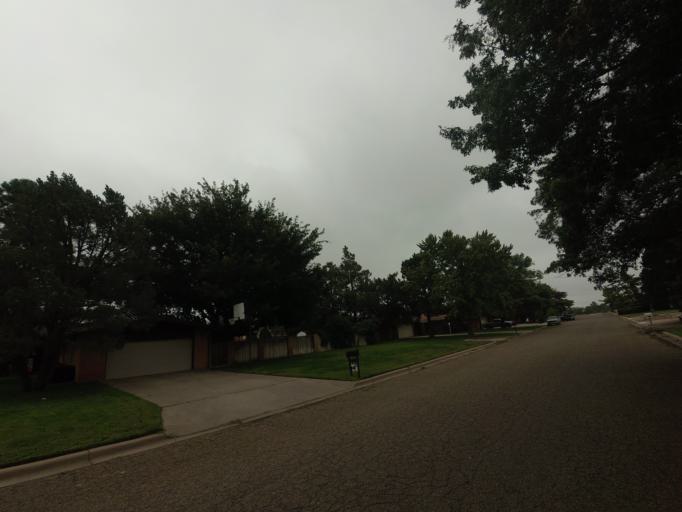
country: US
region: New Mexico
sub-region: Curry County
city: Clovis
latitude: 34.4354
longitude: -103.1905
